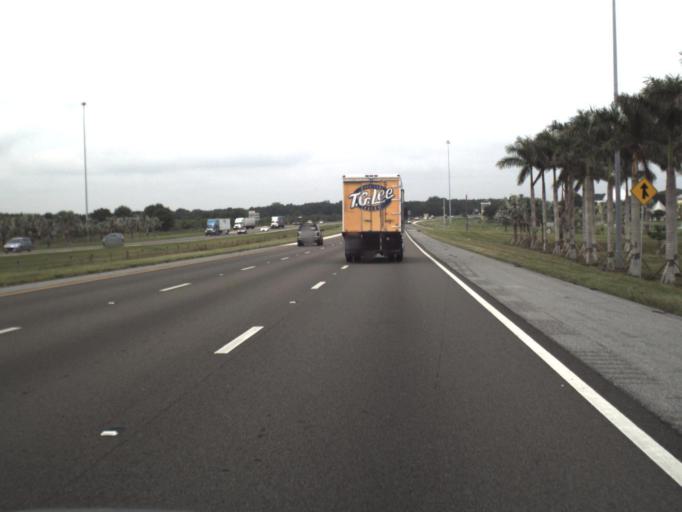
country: US
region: Florida
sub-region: Manatee County
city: Ellenton
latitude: 27.5313
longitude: -82.5084
